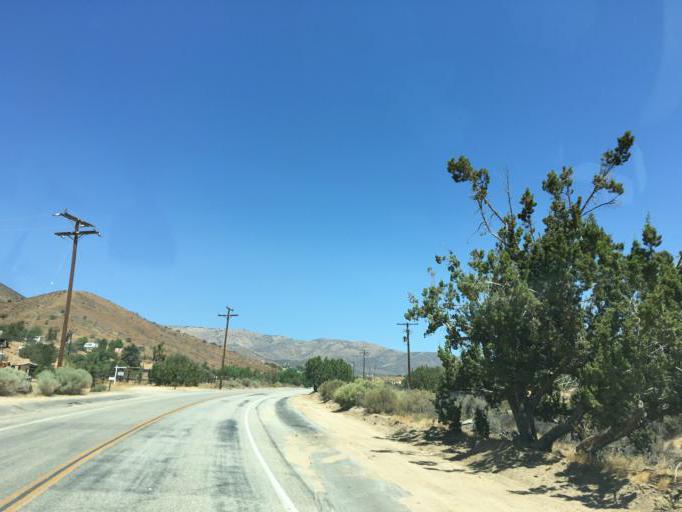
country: US
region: California
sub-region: Los Angeles County
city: Acton
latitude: 34.4995
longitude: -118.2188
